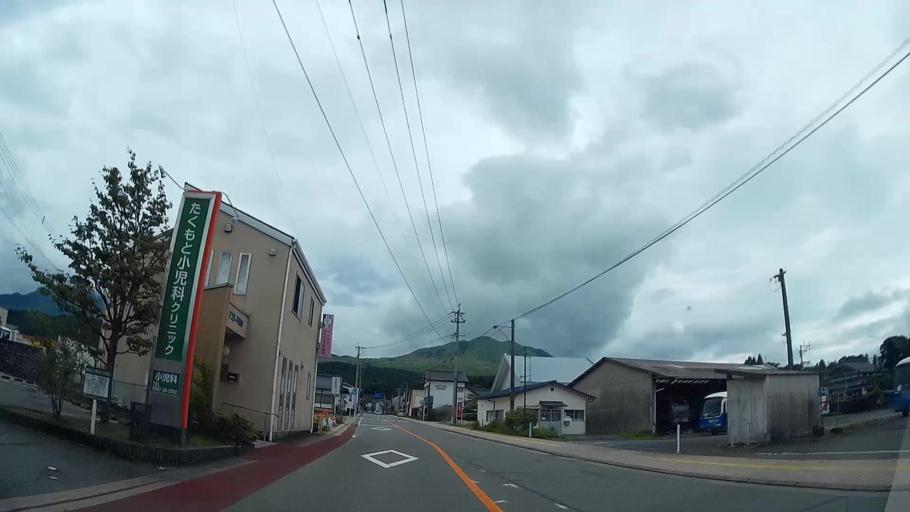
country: JP
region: Kumamoto
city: Aso
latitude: 32.9356
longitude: 131.0802
